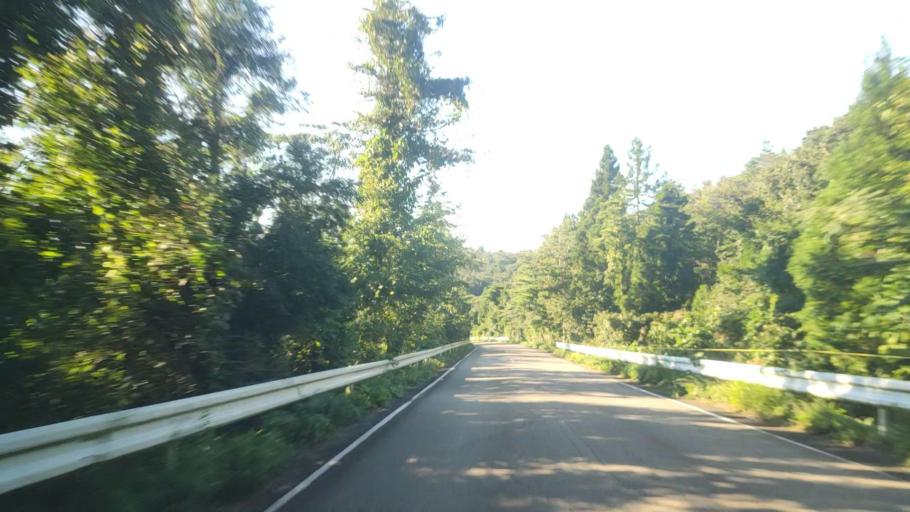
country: JP
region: Ishikawa
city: Nanao
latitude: 37.1188
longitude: 136.9455
